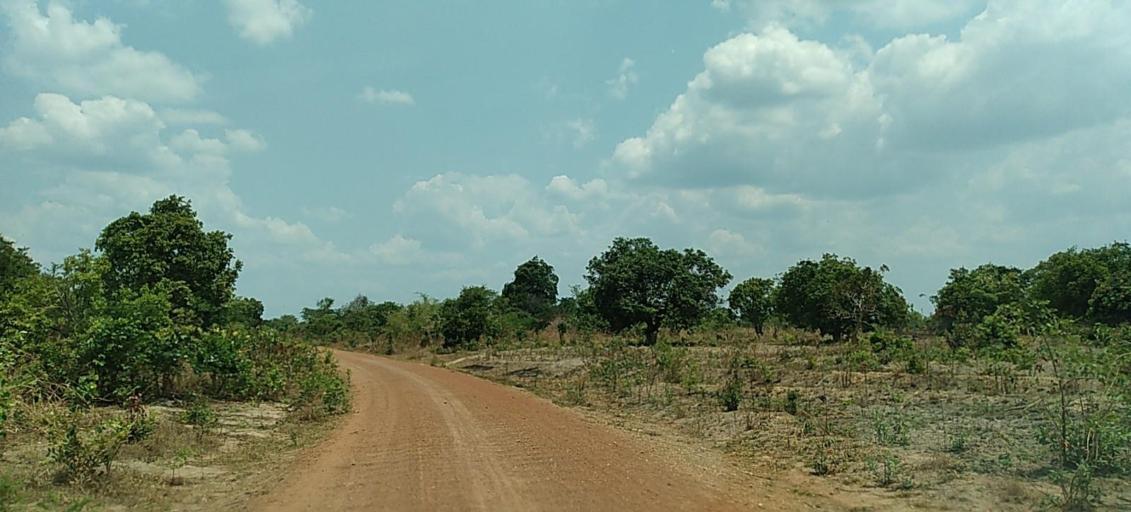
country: ZM
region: Copperbelt
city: Luanshya
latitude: -13.1355
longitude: 28.3131
